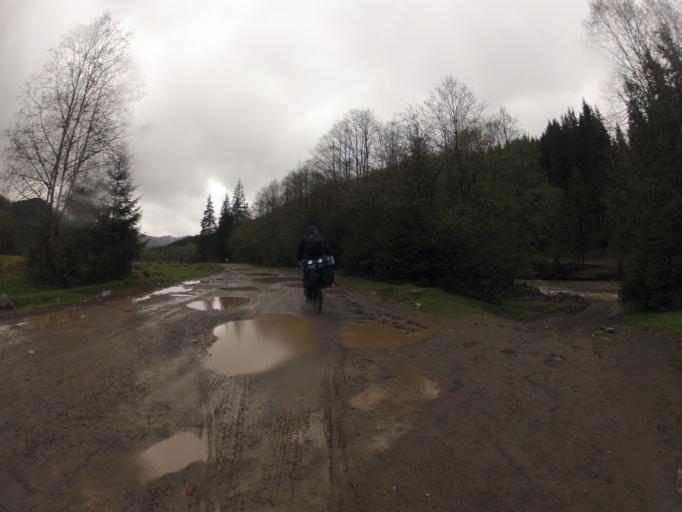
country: RO
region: Suceava
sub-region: Comuna Izvoarele Sucevei
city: Izvoarele Sucevei
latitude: 47.8334
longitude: 25.0564
